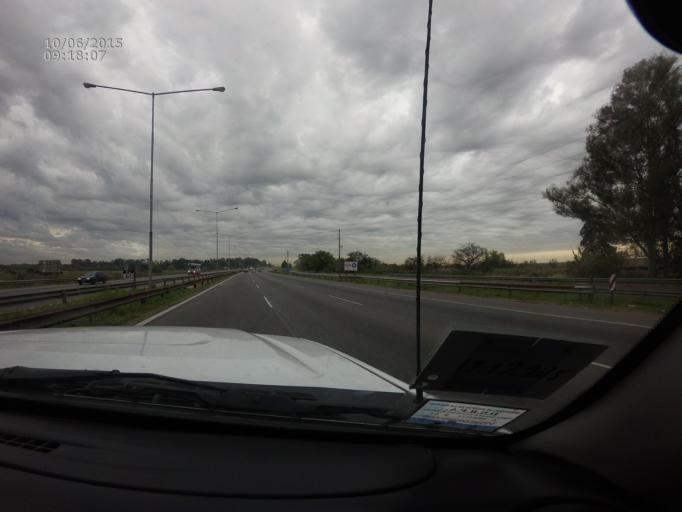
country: AR
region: Buenos Aires
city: Belen de Escobar
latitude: -34.2876
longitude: -58.8898
